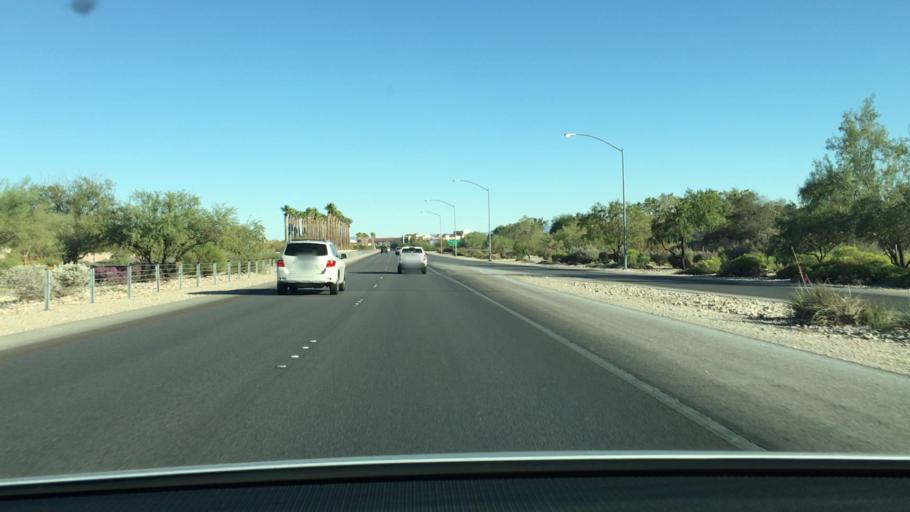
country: US
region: Nevada
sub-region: Clark County
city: Summerlin South
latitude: 36.1846
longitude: -115.3039
